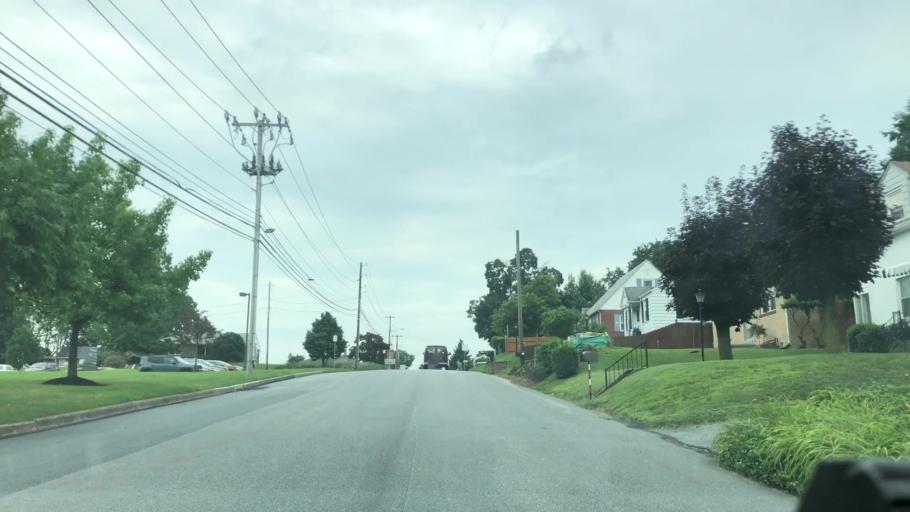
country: US
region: Pennsylvania
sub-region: Dauphin County
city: Colonial Park
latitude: 40.3011
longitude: -76.8110
